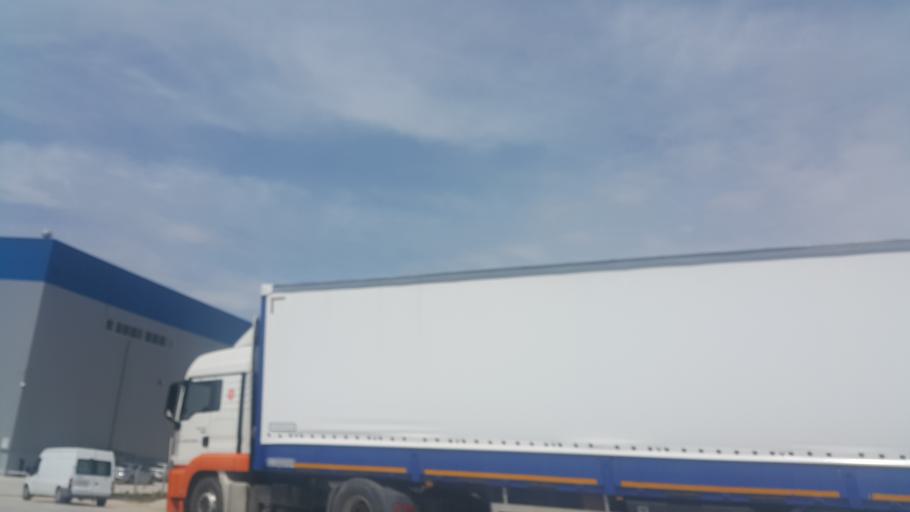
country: TR
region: Adana
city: Yakapinar
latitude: 36.9686
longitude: 35.5496
